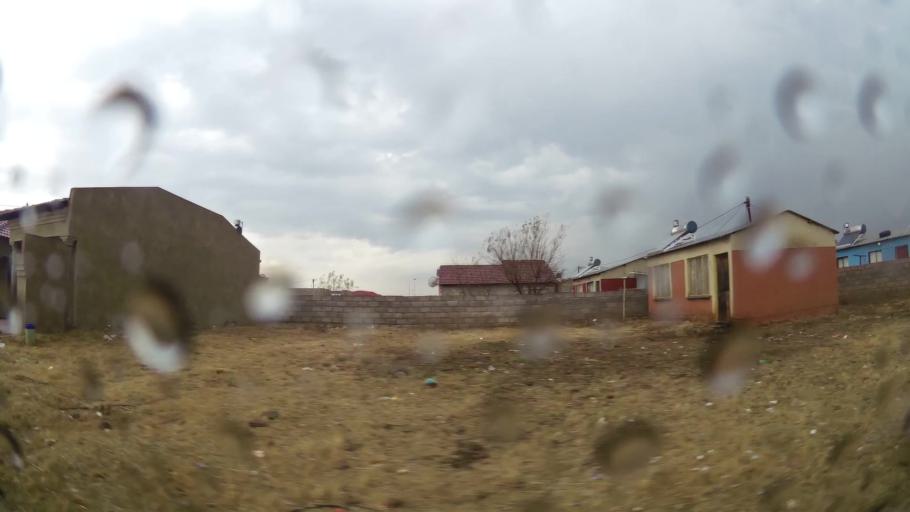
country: ZA
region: Gauteng
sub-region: Ekurhuleni Metropolitan Municipality
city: Germiston
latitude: -26.3740
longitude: 28.1472
